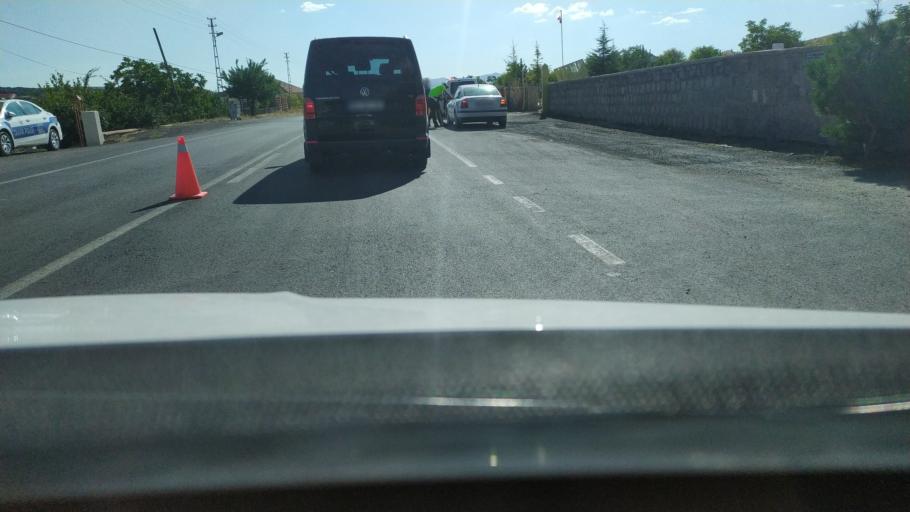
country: TR
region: Kayseri
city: Felahiye
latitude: 39.1065
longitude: 35.5986
